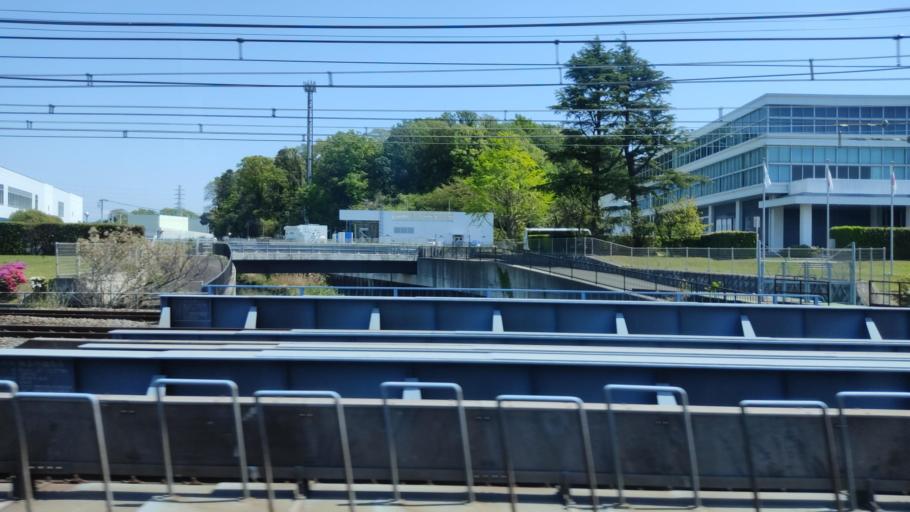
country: JP
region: Kanagawa
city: Kamakura
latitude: 35.3643
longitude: 139.5302
